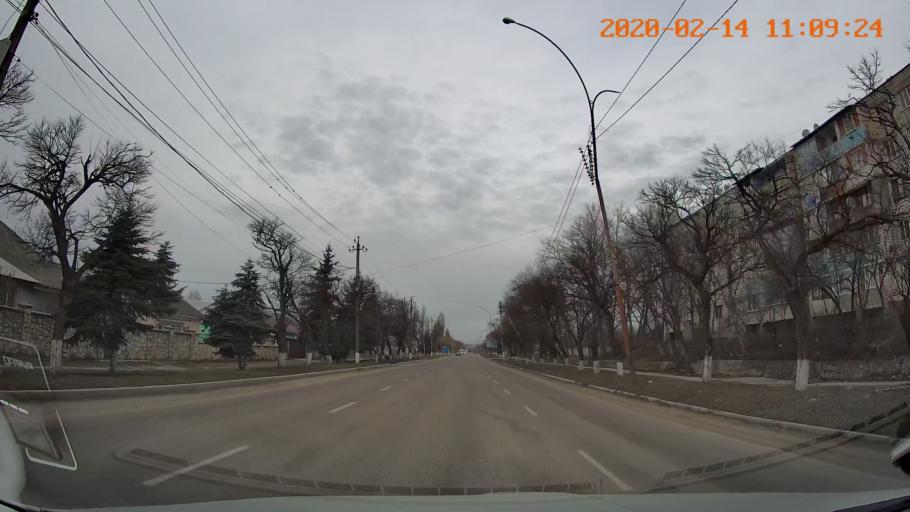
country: MD
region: Raionul Edinet
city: Edinet
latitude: 48.1780
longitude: 27.2944
